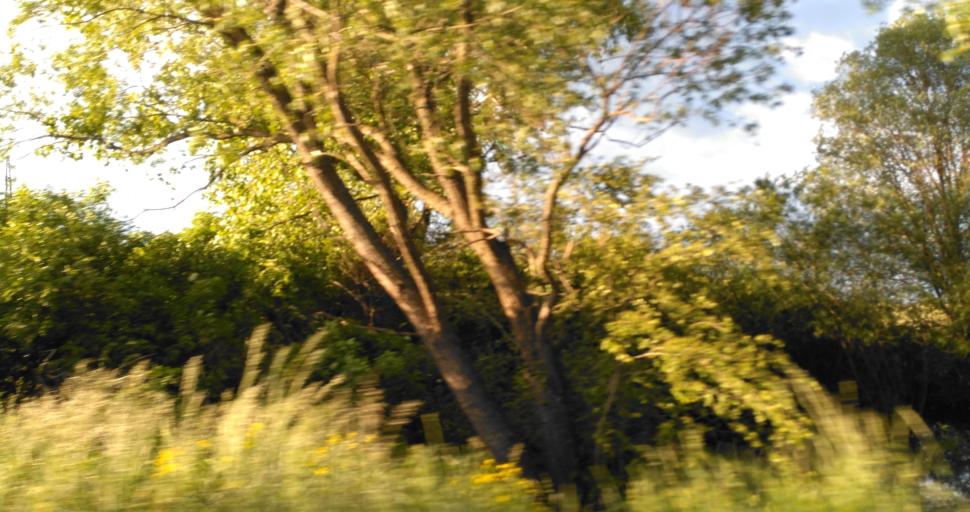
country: CZ
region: Central Bohemia
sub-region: Okres Beroun
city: Beroun
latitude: 49.9242
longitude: 14.0957
